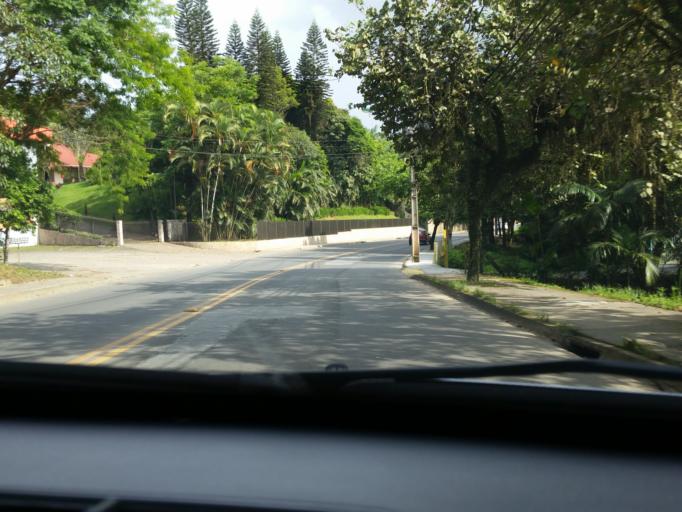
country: BR
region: Santa Catarina
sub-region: Blumenau
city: Blumenau
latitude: -26.9032
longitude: -49.1329
